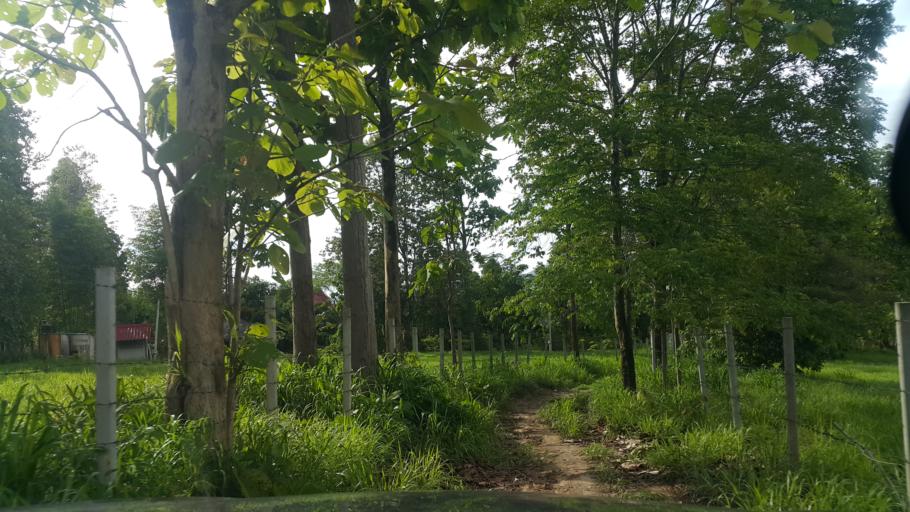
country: TH
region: Chiang Mai
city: Mae On
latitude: 18.7089
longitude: 99.2157
